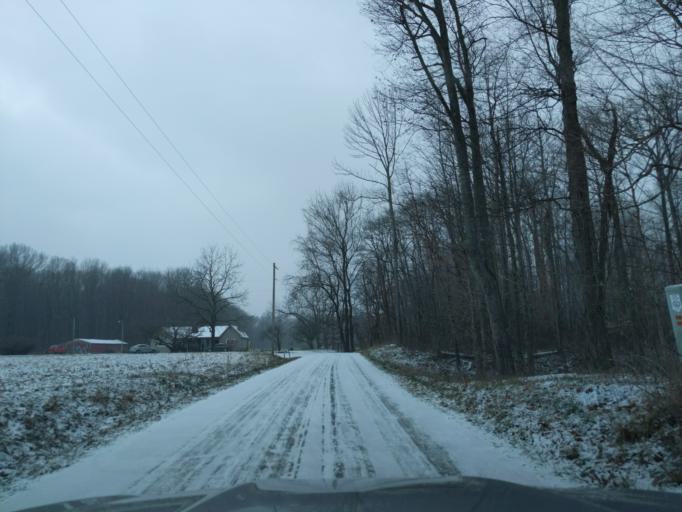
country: US
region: Indiana
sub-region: Decatur County
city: Westport
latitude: 39.2339
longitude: -85.4929
